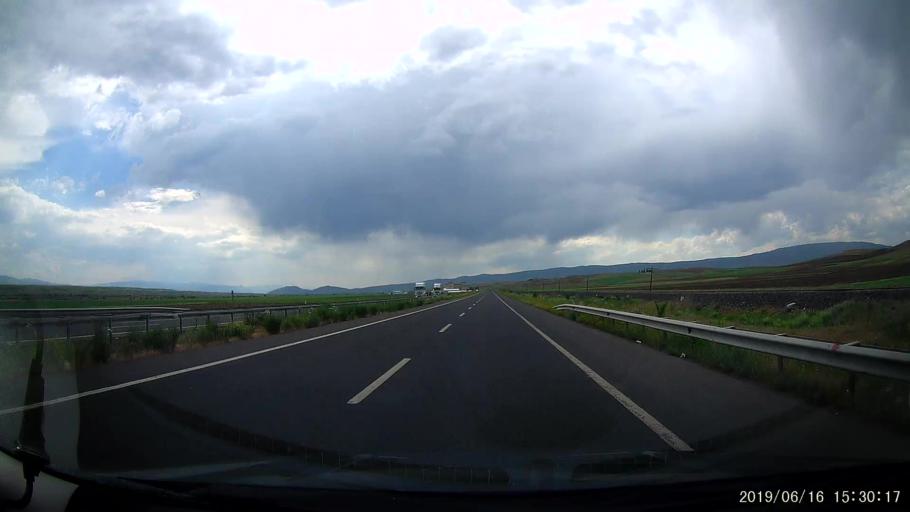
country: TR
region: Erzurum
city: Horasan
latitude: 40.0334
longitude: 42.1096
